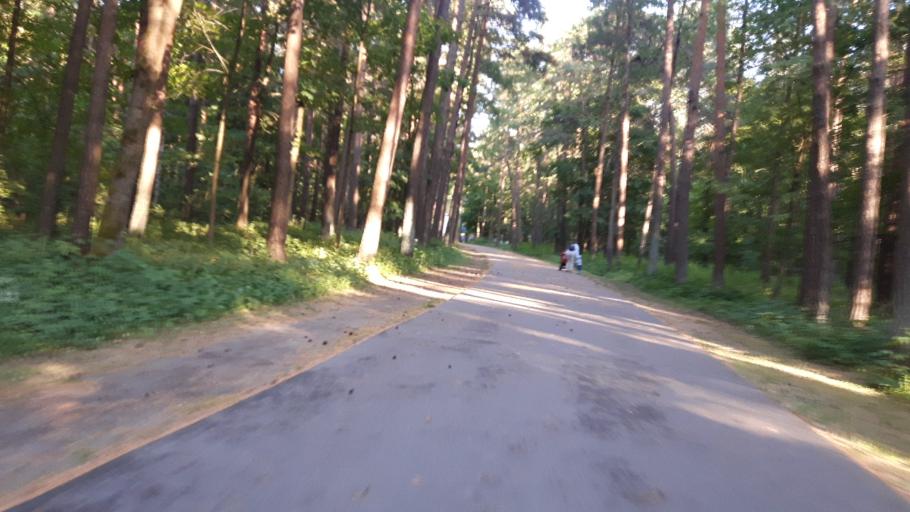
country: LV
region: Riga
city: Jaunciems
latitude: 57.0015
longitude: 24.1456
